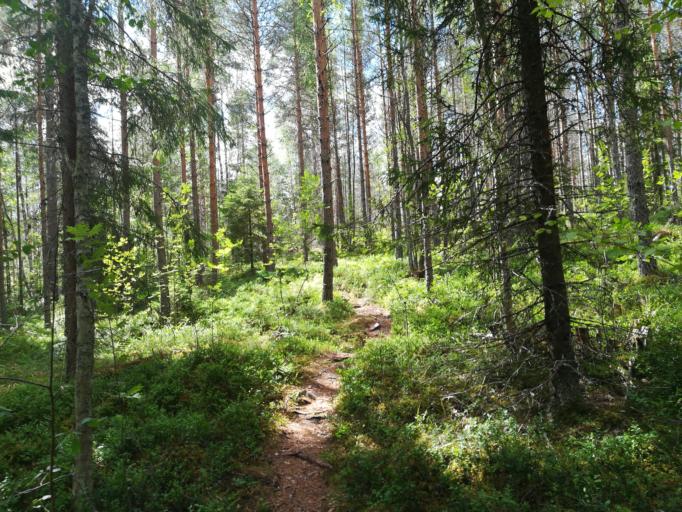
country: FI
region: Southern Savonia
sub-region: Mikkeli
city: Maentyharju
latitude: 61.3638
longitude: 26.9342
